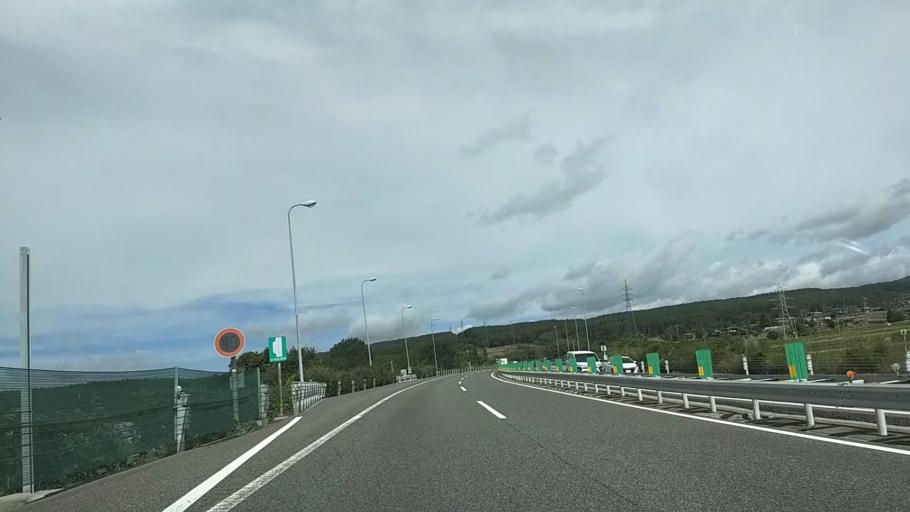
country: JP
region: Nagano
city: Chino
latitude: 35.8812
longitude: 138.3011
